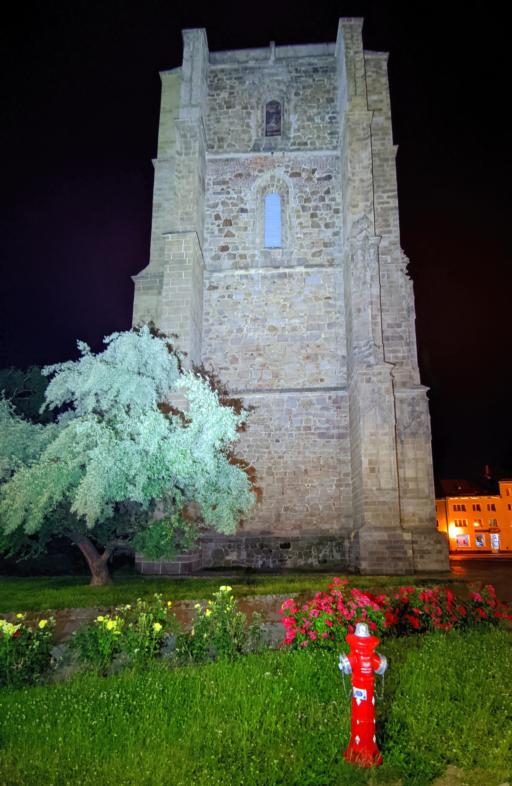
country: PL
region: Opole Voivodeship
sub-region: Powiat nyski
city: Nysa
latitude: 50.4748
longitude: 17.3338
